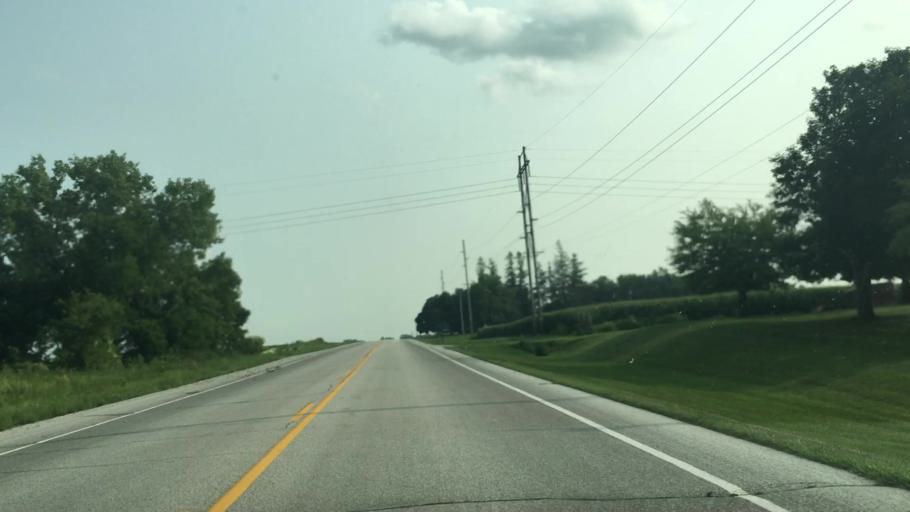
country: US
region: Minnesota
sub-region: Fillmore County
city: Harmony
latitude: 43.5519
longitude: -91.9297
